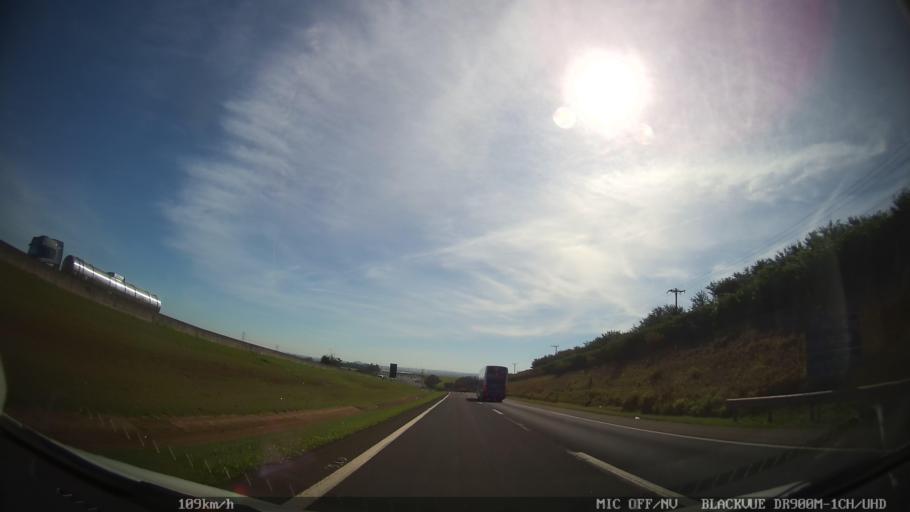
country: BR
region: Sao Paulo
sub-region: Leme
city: Leme
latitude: -22.2575
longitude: -47.3900
